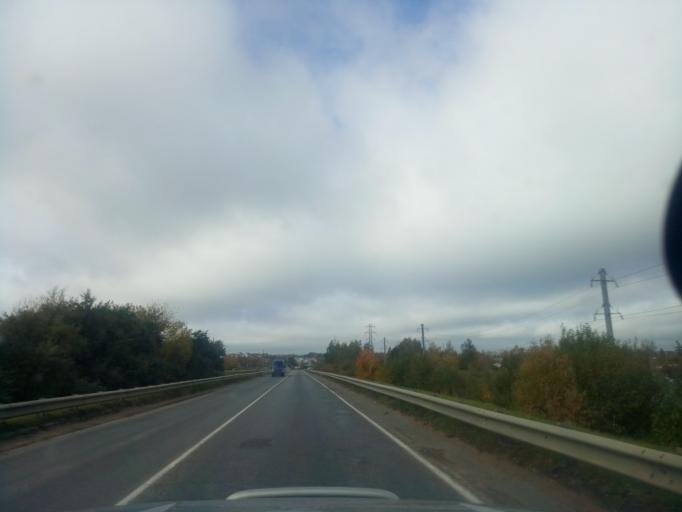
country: BY
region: Minsk
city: Zaslawye
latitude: 53.9997
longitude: 27.2814
